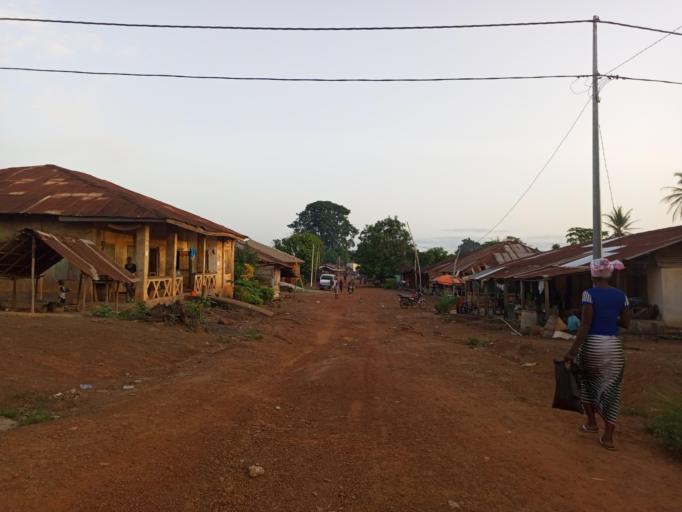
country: SL
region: Eastern Province
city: Pendembu
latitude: 8.0981
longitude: -10.6946
